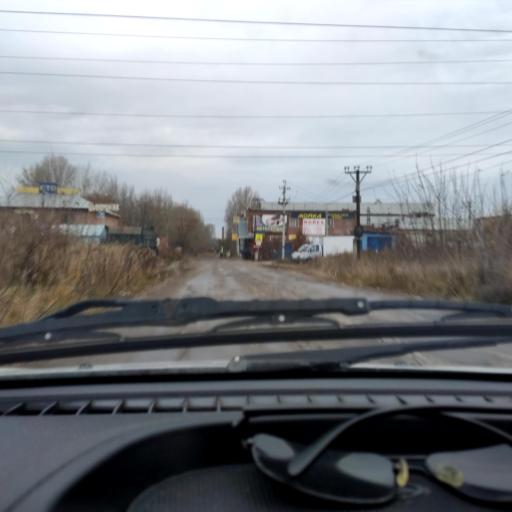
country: RU
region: Samara
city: Tol'yatti
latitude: 53.5167
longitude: 49.4651
